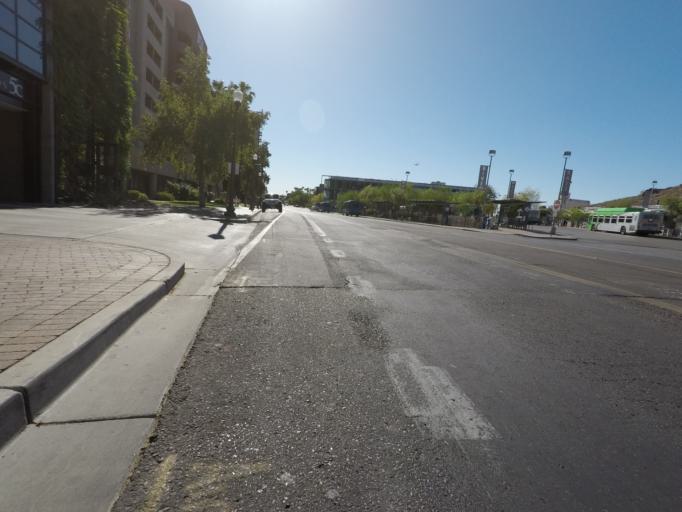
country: US
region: Arizona
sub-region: Maricopa County
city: Tempe Junction
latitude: 33.4255
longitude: -111.9352
